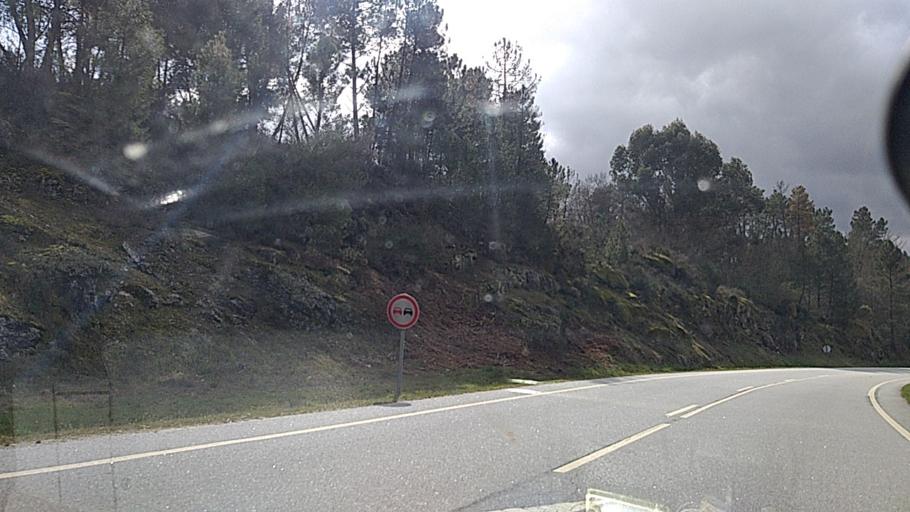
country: PT
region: Viseu
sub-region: Mangualde
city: Mangualde
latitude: 40.6512
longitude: -7.7329
